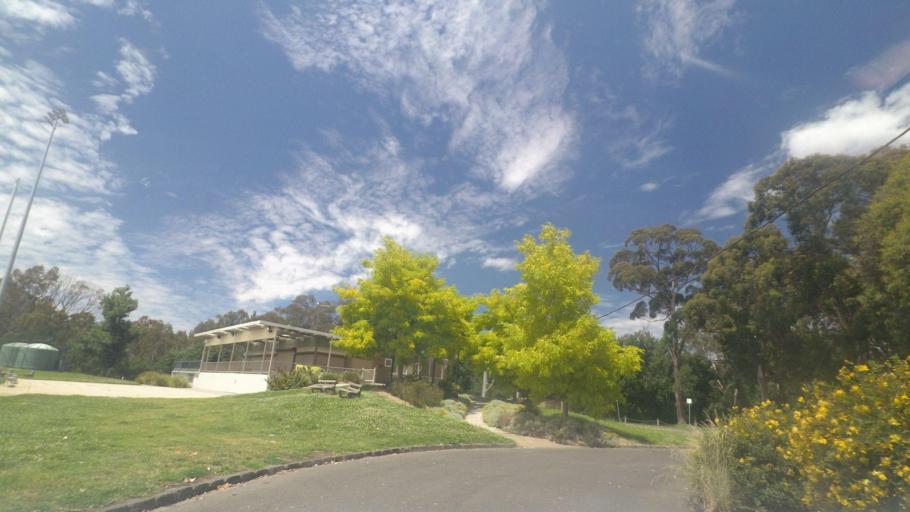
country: AU
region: Victoria
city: Rosanna
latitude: -37.7560
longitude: 145.0745
